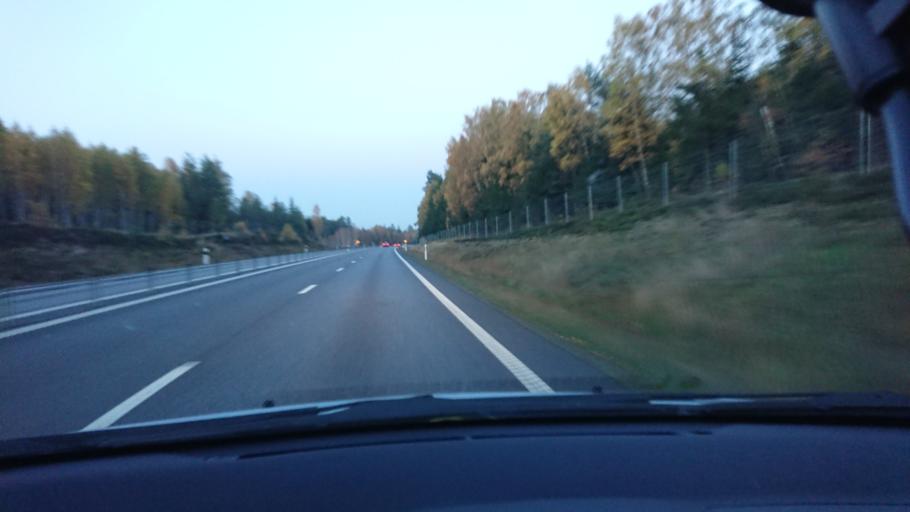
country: SE
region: Kronoberg
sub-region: Ljungby Kommun
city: Ljungby
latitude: 56.7829
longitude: 13.8227
